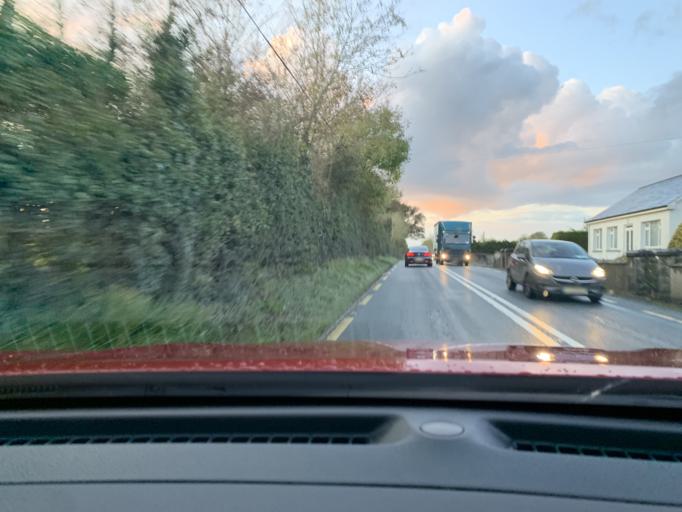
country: IE
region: Connaught
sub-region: Sligo
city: Ballymote
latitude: 54.1036
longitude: -8.4089
